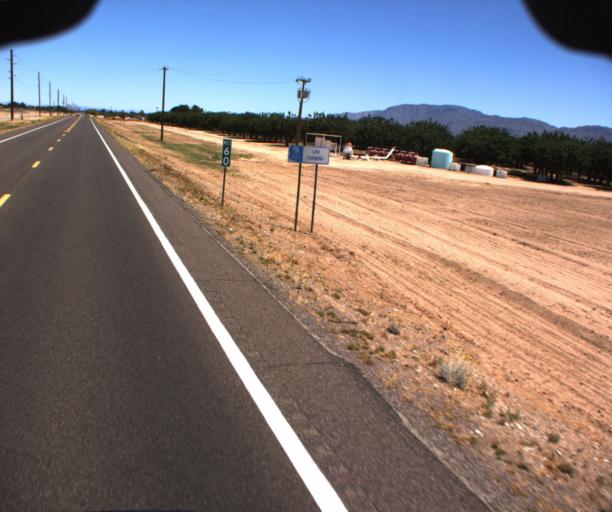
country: US
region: Arizona
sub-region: La Paz County
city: Salome
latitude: 33.8103
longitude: -113.5630
